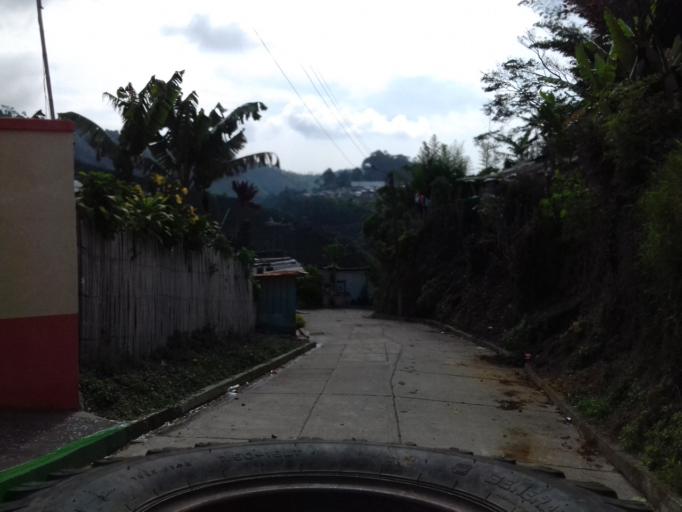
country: CO
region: Tolima
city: Libano
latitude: 4.9240
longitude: -75.0568
